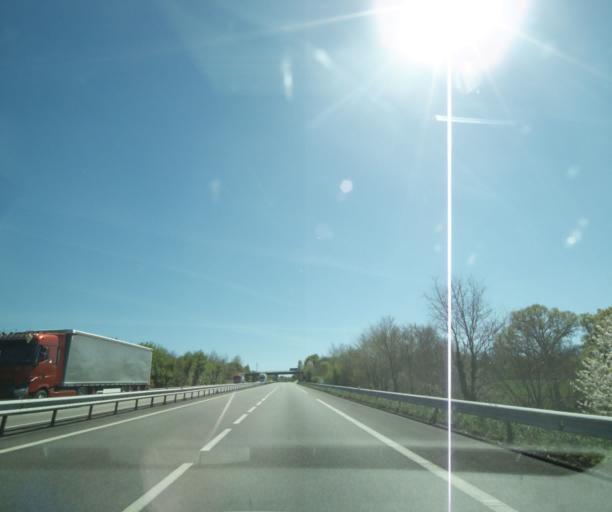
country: FR
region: Limousin
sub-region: Departement de la Haute-Vienne
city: Saint-Germain-les-Belles
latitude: 45.5454
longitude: 1.5093
